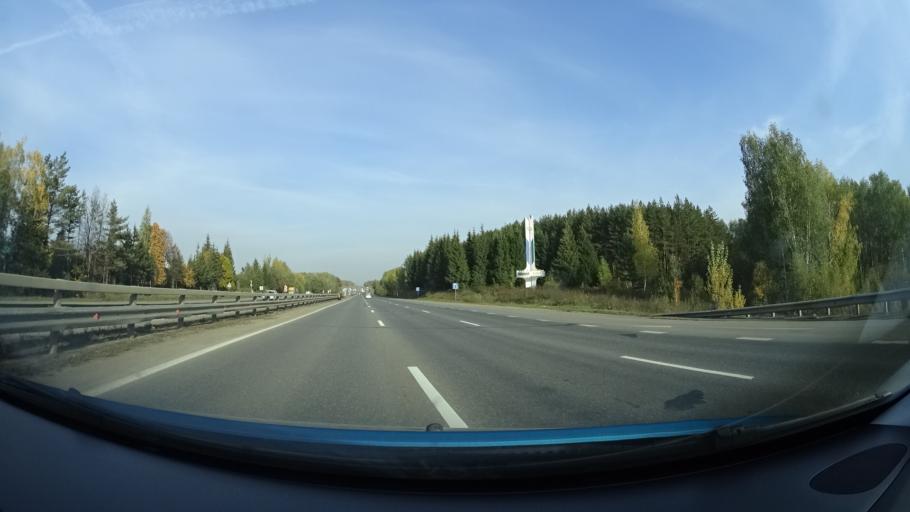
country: RU
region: Bashkortostan
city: Avdon
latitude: 54.6476
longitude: 55.6442
